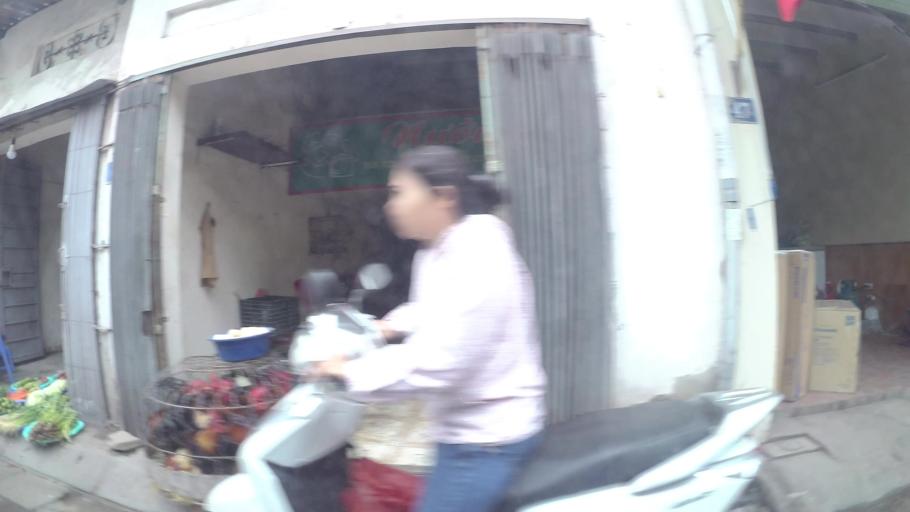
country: VN
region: Ha Noi
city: Hai BaTrung
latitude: 20.9916
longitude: 105.8887
